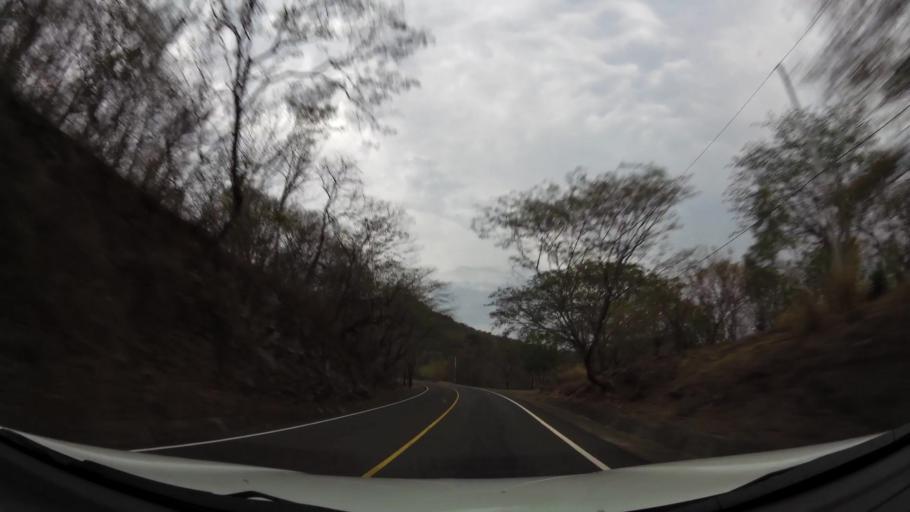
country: NI
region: Esteli
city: Esteli
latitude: 12.9948
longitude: -86.2721
